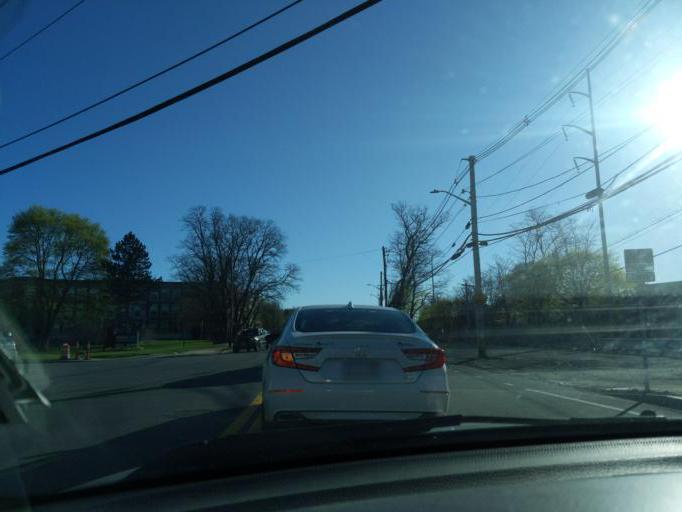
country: US
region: Massachusetts
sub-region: Essex County
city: Beverly
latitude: 42.5582
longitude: -70.8801
